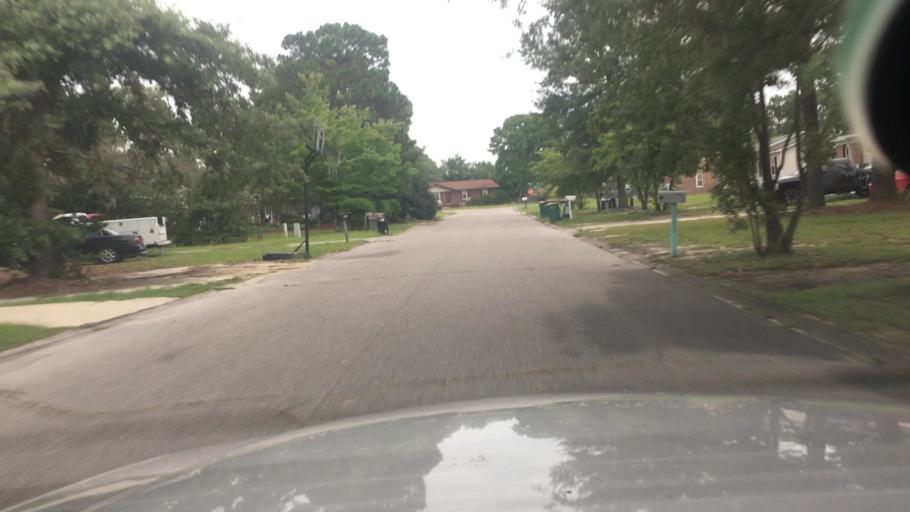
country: US
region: North Carolina
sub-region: Cumberland County
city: Hope Mills
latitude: 34.9717
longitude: -78.9712
